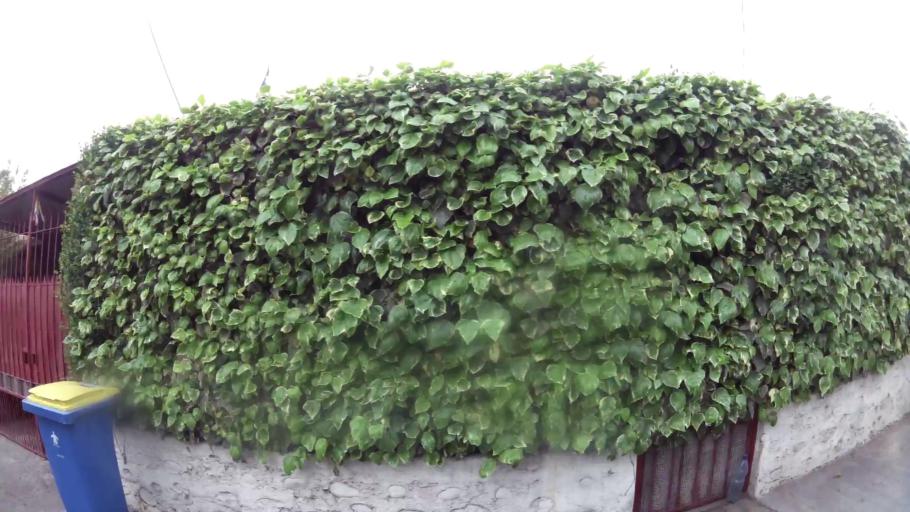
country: CL
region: Santiago Metropolitan
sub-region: Provincia de Santiago
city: Villa Presidente Frei, Nunoa, Santiago, Chile
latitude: -33.5133
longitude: -70.5960
